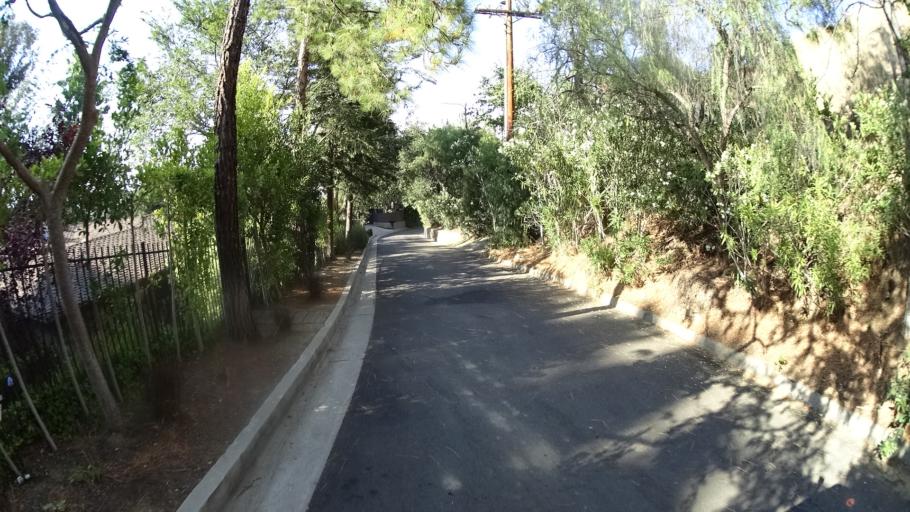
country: US
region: California
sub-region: Los Angeles County
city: Universal City
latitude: 34.1251
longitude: -118.3893
